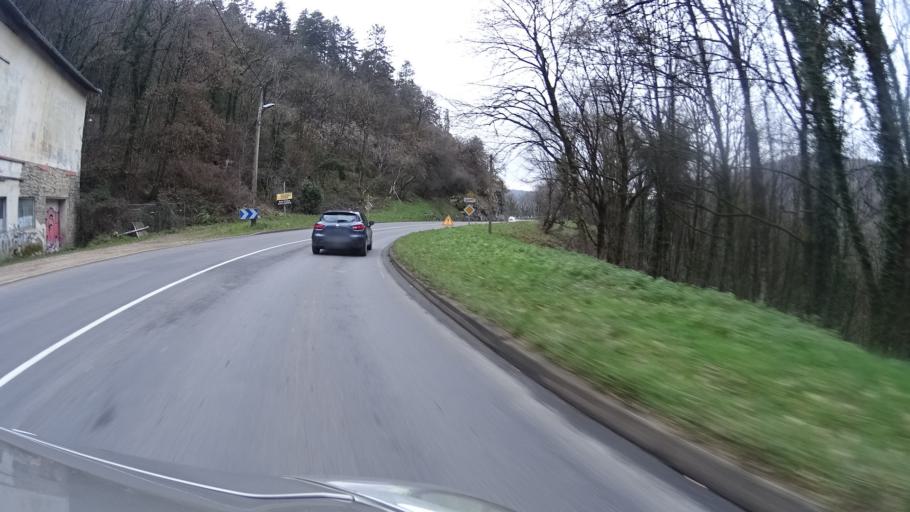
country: FR
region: Franche-Comte
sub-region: Departement du Doubs
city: Morre
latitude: 47.2275
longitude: 6.0626
